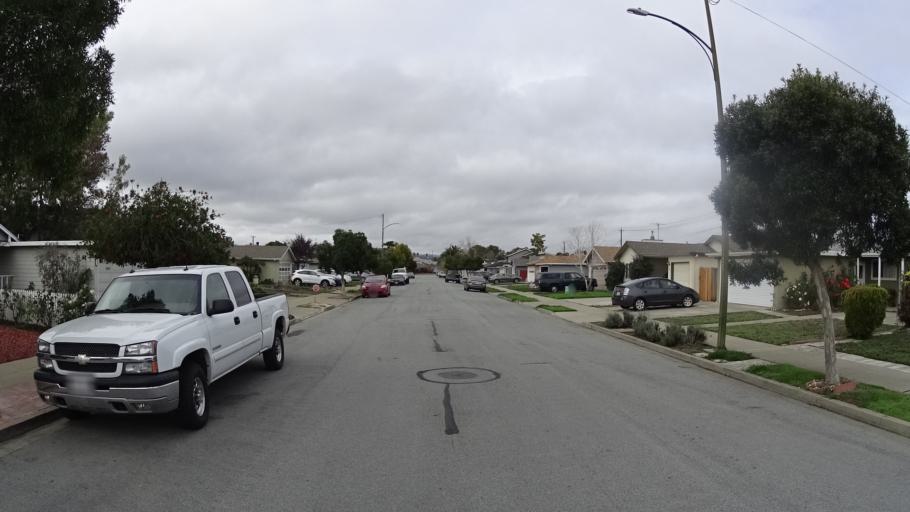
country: US
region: California
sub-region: San Mateo County
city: Belmont
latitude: 37.5293
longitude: -122.2816
